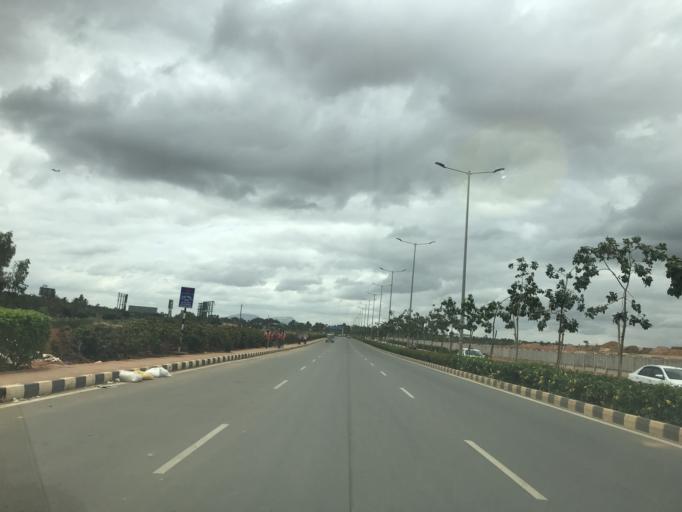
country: IN
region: Karnataka
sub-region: Bangalore Rural
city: Devanhalli
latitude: 13.1889
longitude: 77.6805
